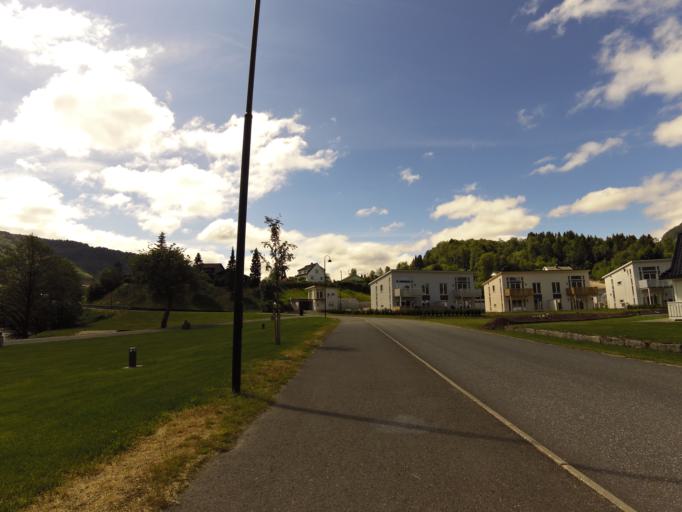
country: NO
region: Vest-Agder
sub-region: Kvinesdal
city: Liknes
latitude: 58.3136
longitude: 6.9592
